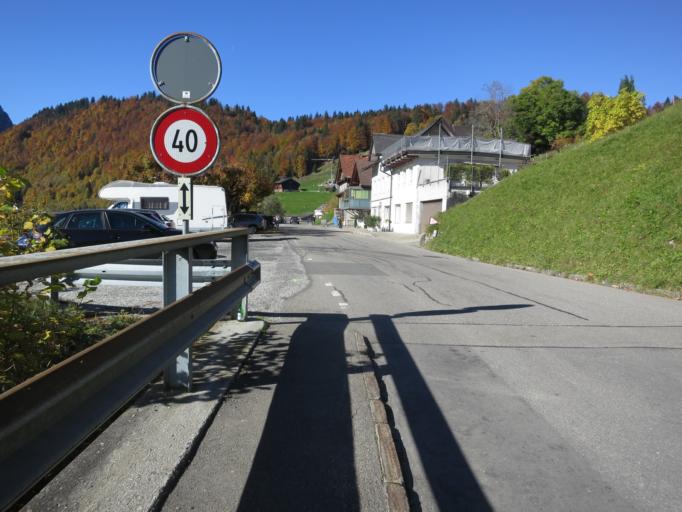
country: CH
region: Schwyz
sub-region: Bezirk March
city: Vorderthal
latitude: 47.1032
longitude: 8.9206
